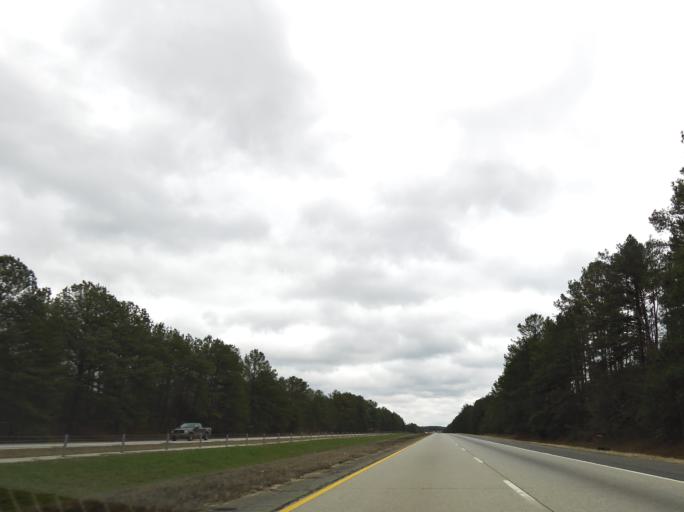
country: US
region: Georgia
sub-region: Houston County
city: Warner Robins
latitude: 32.7358
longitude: -83.5410
